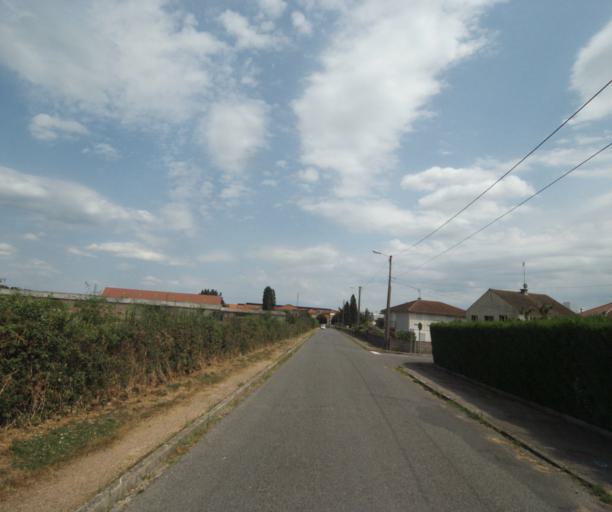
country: FR
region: Bourgogne
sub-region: Departement de Saone-et-Loire
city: Gueugnon
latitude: 46.6079
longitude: 4.0591
